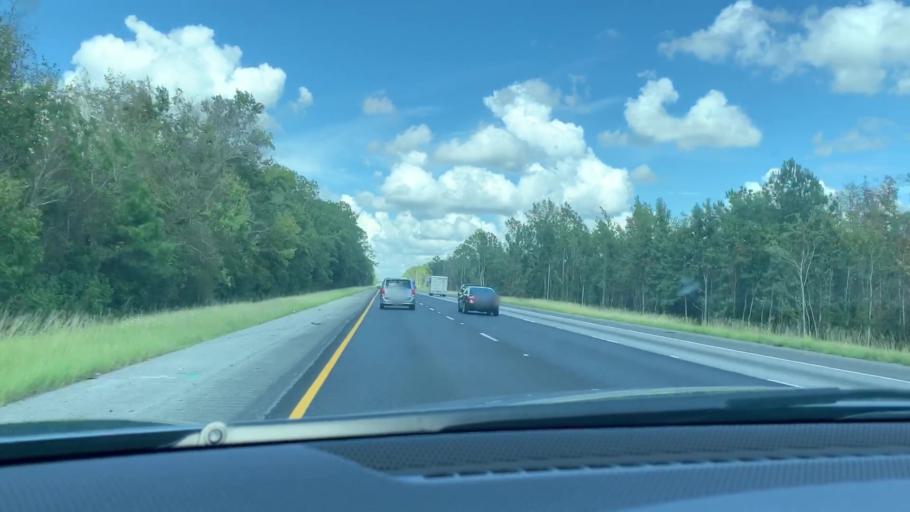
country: US
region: Georgia
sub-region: Camden County
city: Woodbine
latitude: 30.9158
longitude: -81.6859
